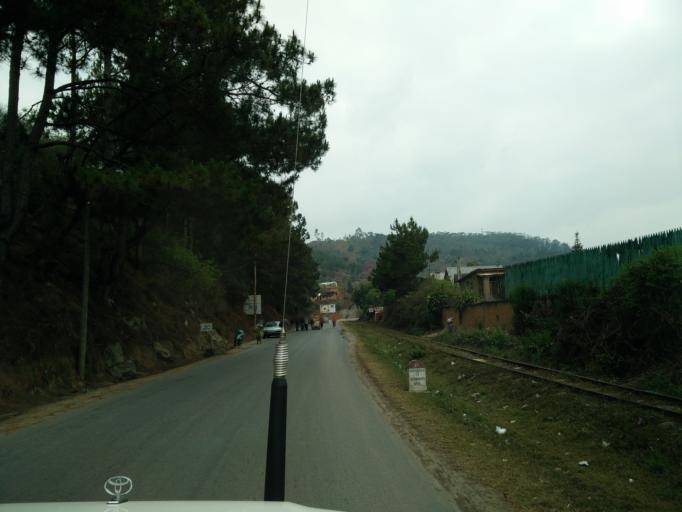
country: MG
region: Upper Matsiatra
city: Fianarantsoa
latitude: -21.4280
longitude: 47.1268
